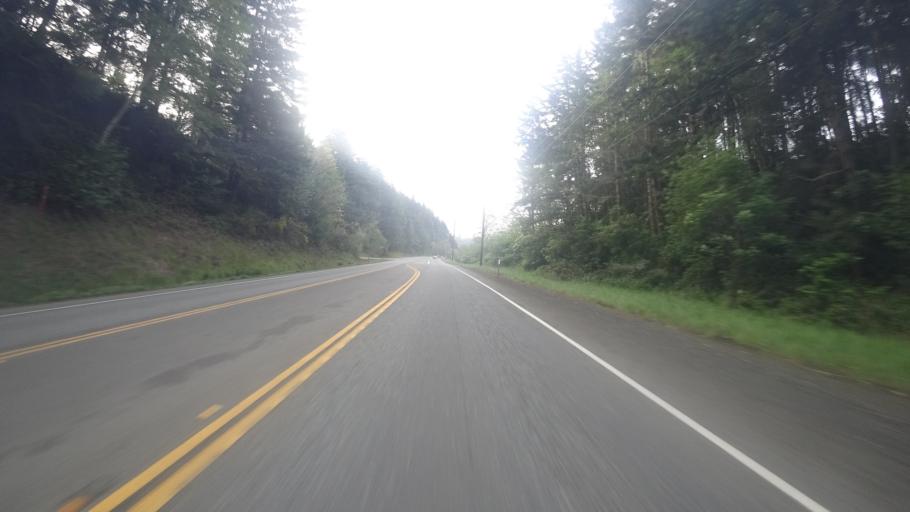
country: US
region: Oregon
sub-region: Coos County
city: North Bend
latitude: 43.4537
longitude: -124.2280
